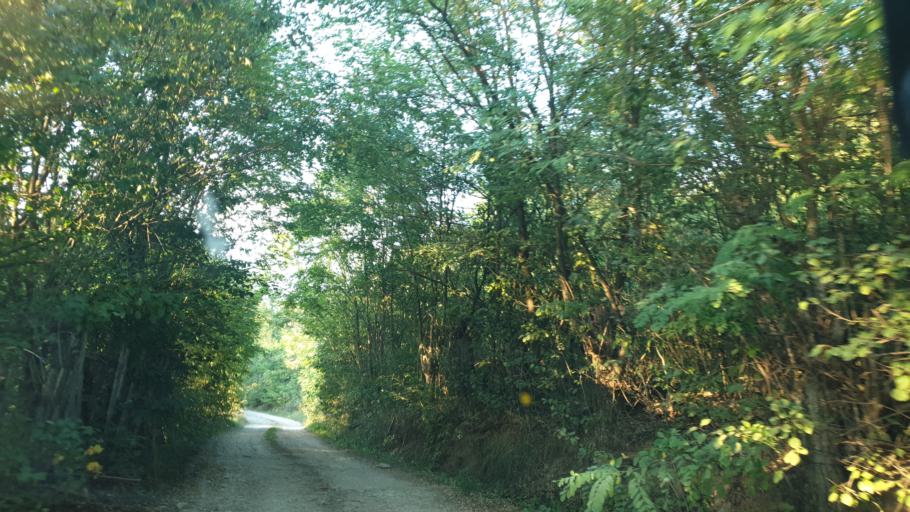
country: RS
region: Central Serbia
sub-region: Zlatiborski Okrug
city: Kosjeric
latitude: 43.9990
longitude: 20.0033
